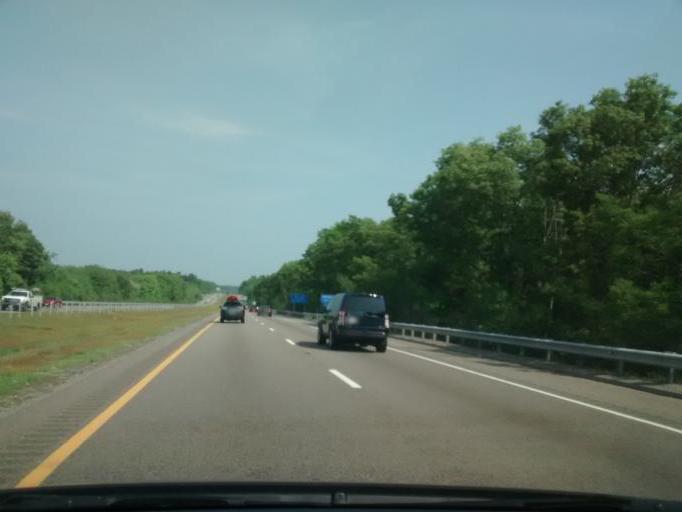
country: US
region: Massachusetts
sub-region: Plymouth County
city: Middleborough Center
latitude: 41.8807
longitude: -70.9173
